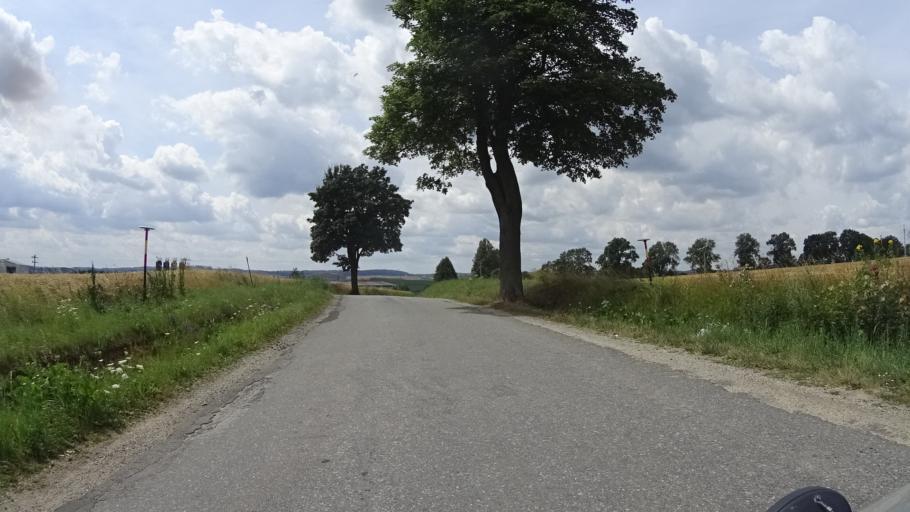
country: CZ
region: Vysocina
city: Merin
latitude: 49.4027
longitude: 15.9160
